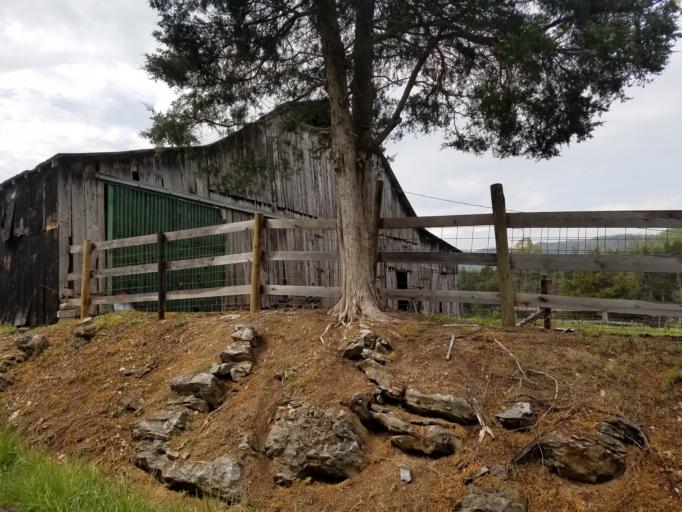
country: US
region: Virginia
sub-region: Lee County
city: Jonesville
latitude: 36.7127
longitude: -83.1752
